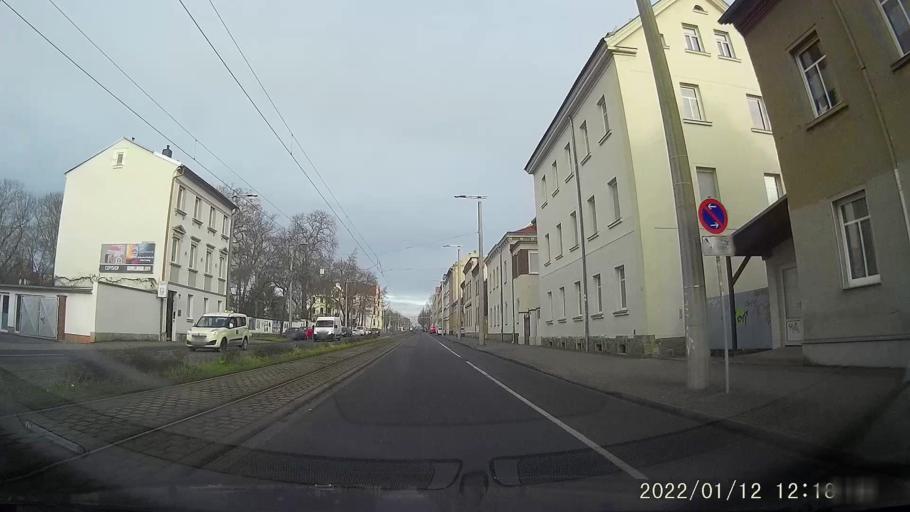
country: DE
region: Saxony
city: Kodersdorf
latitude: 51.2208
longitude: 14.8914
